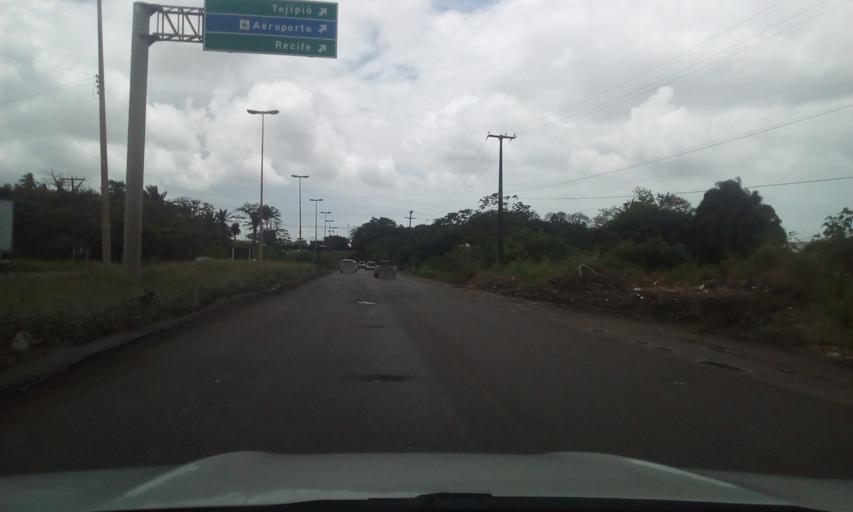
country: BR
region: Pernambuco
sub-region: Jaboatao Dos Guararapes
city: Jaboatao dos Guararapes
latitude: -8.0955
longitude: -34.9490
